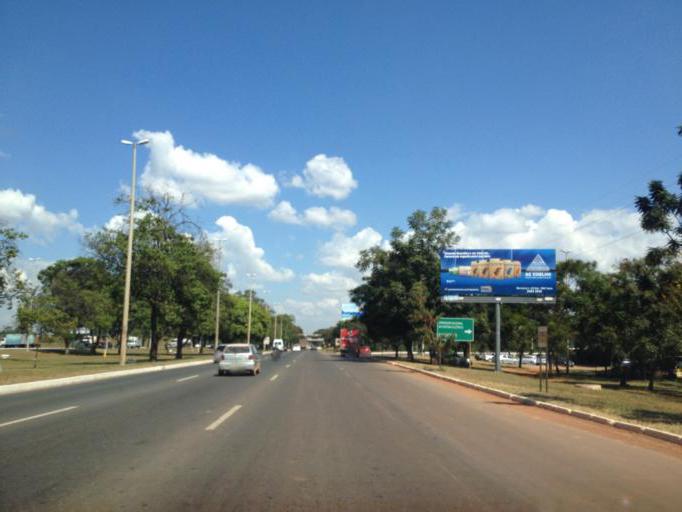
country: BR
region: Federal District
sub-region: Brasilia
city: Brasilia
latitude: -15.8049
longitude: -47.9478
